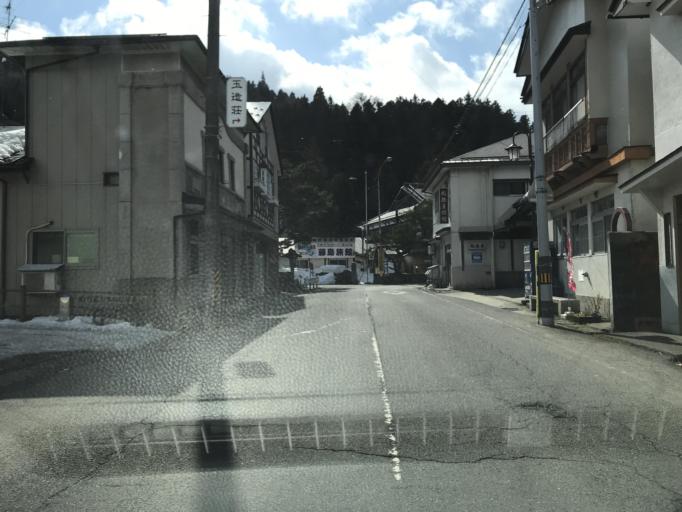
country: JP
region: Miyagi
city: Furukawa
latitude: 38.7315
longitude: 140.7681
